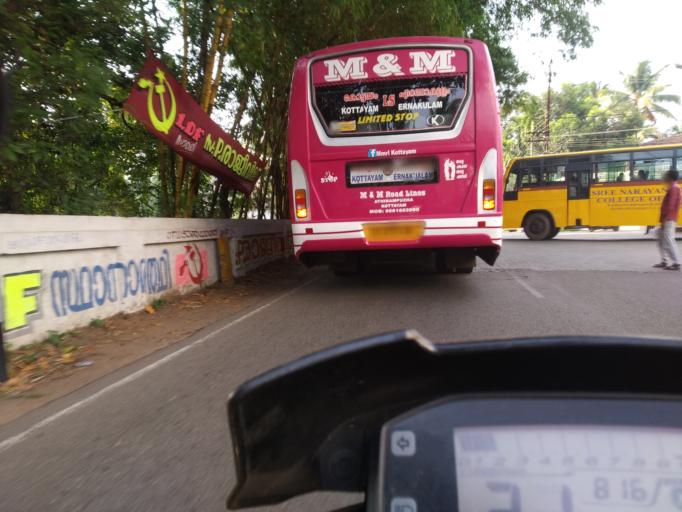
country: IN
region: Kerala
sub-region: Alappuzha
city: Arukutti
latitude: 9.9388
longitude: 76.3515
